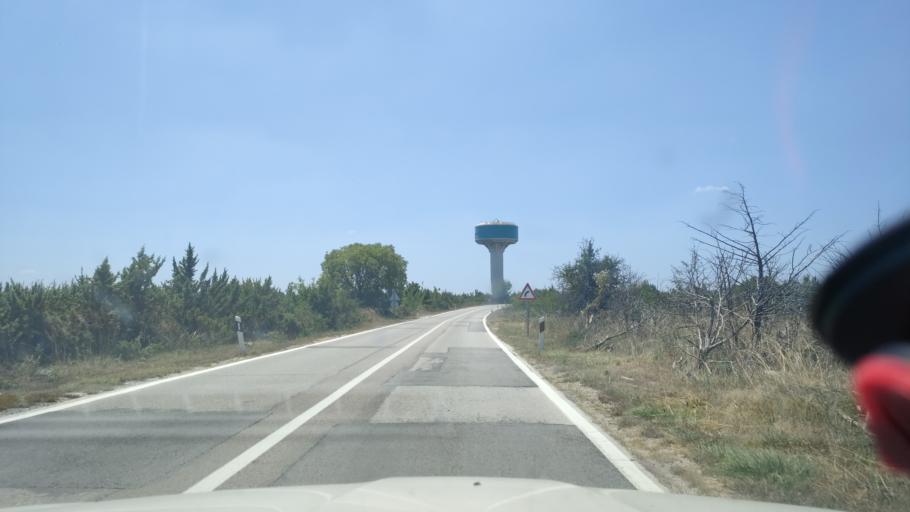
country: HR
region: Sibensko-Kniniska
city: Kistanje
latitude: 43.9965
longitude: 15.9828
